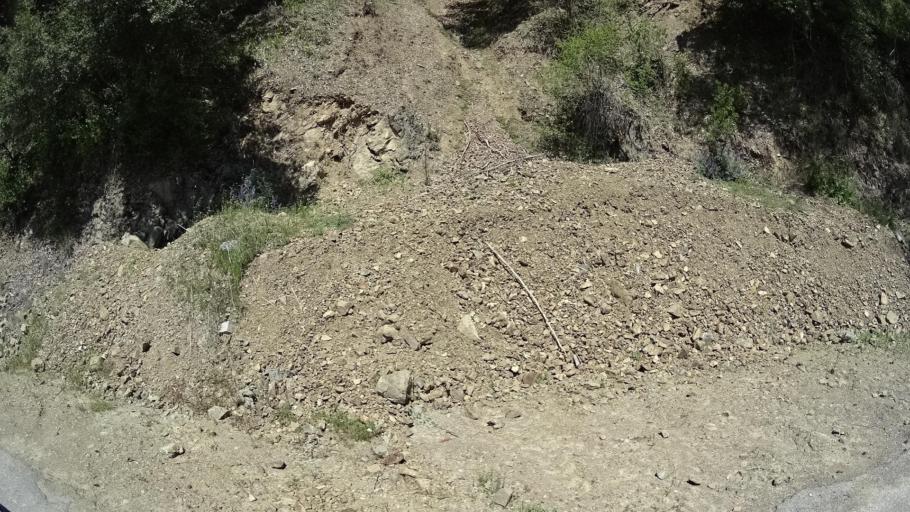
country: US
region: California
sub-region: Humboldt County
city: Redway
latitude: 40.1928
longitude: -123.5427
